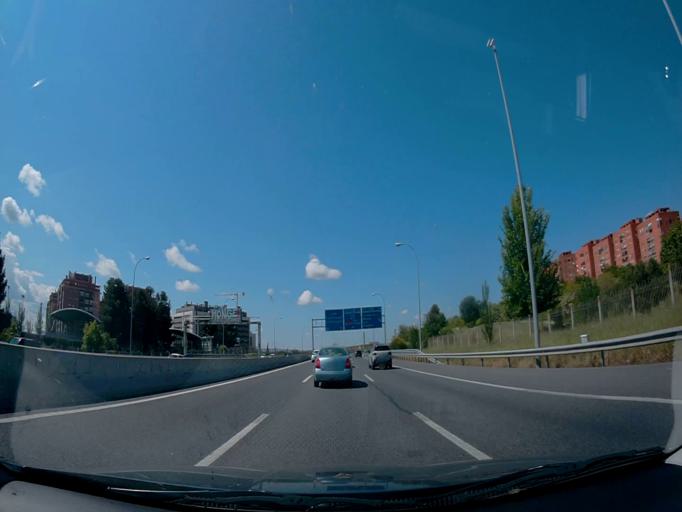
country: ES
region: Madrid
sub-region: Provincia de Madrid
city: Puente de Vallecas
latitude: 40.3830
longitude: -3.6371
